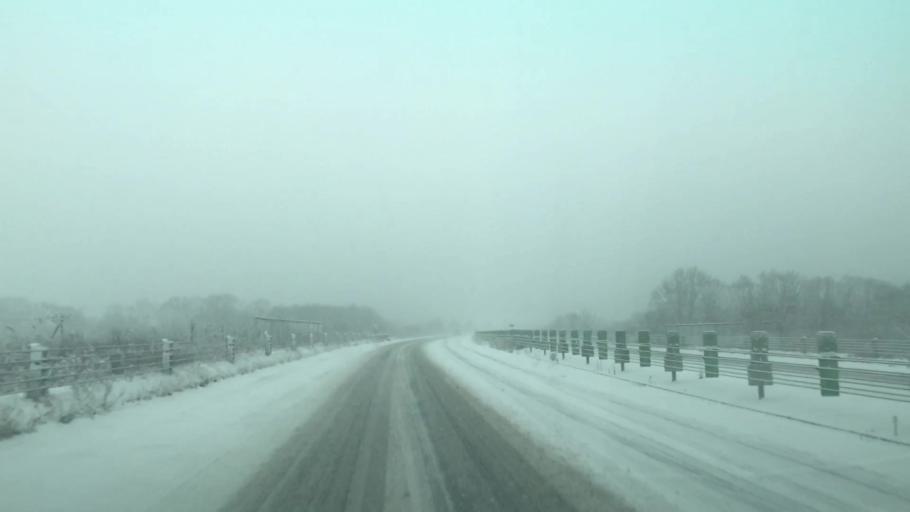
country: JP
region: Hokkaido
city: Shiraoi
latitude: 42.5083
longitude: 141.2695
